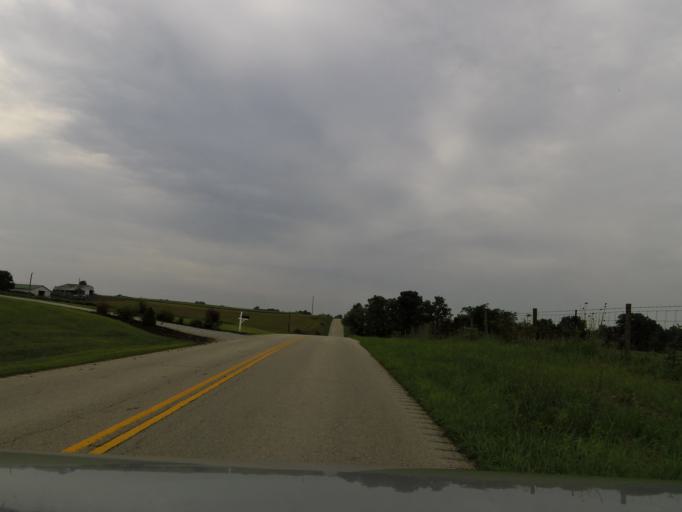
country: US
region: Kentucky
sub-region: Robertson County
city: Mount Olivet
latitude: 38.5136
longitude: -83.8997
